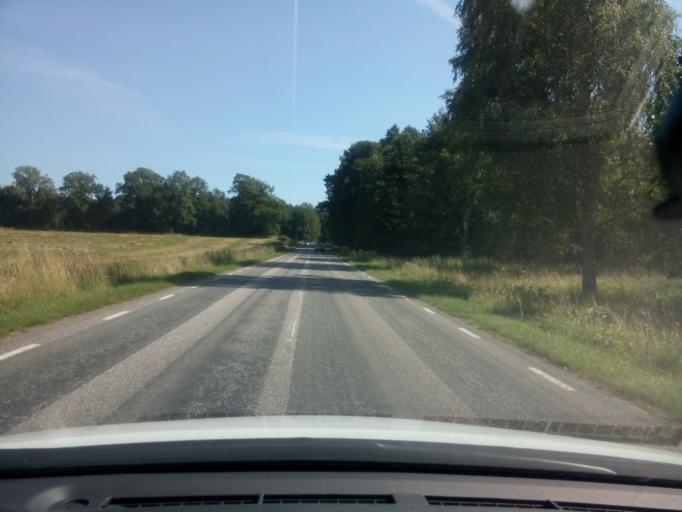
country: SE
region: Soedermanland
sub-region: Oxelosunds Kommun
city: Oxelosund
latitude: 58.7592
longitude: 17.2954
